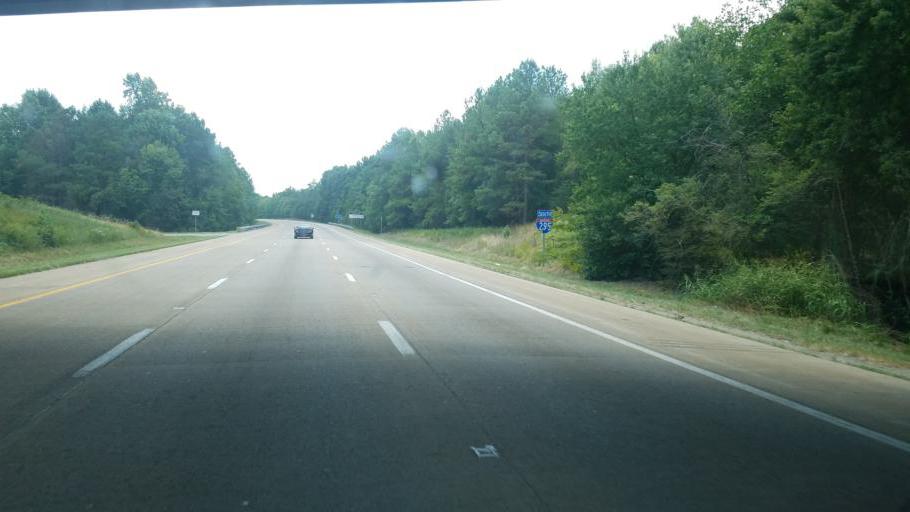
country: US
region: Virginia
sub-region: Henrico County
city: Fort Lee
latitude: 37.4300
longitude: -77.3400
